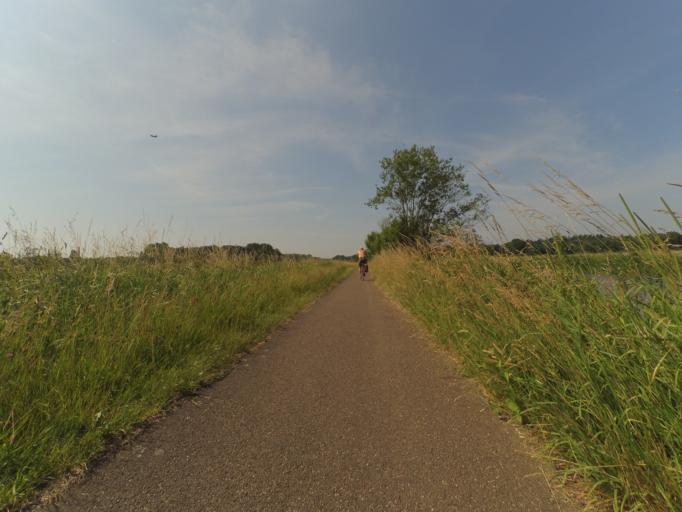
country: NL
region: North Brabant
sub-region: Gemeente Breda
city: Breda
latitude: 51.5347
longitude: 4.7812
